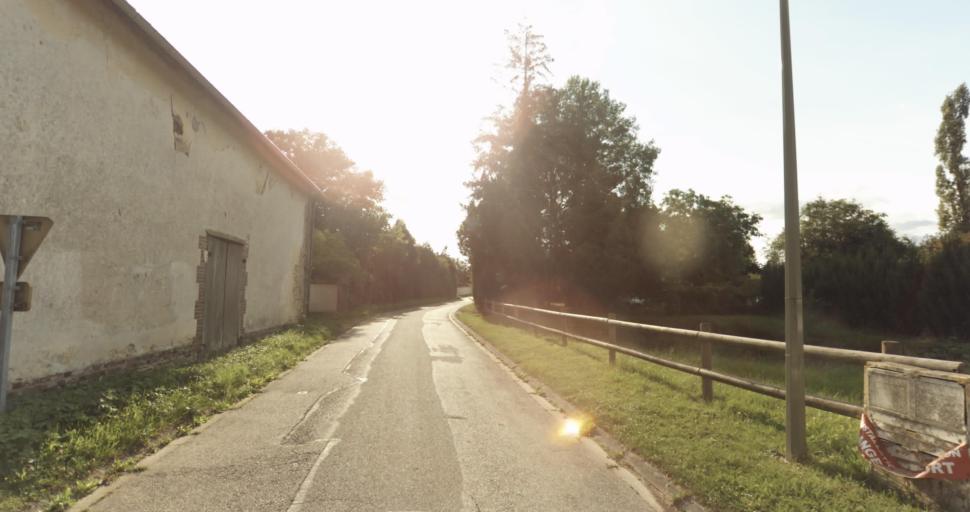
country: FR
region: Haute-Normandie
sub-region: Departement de l'Eure
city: La Couture-Boussey
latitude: 48.8961
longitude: 1.3591
